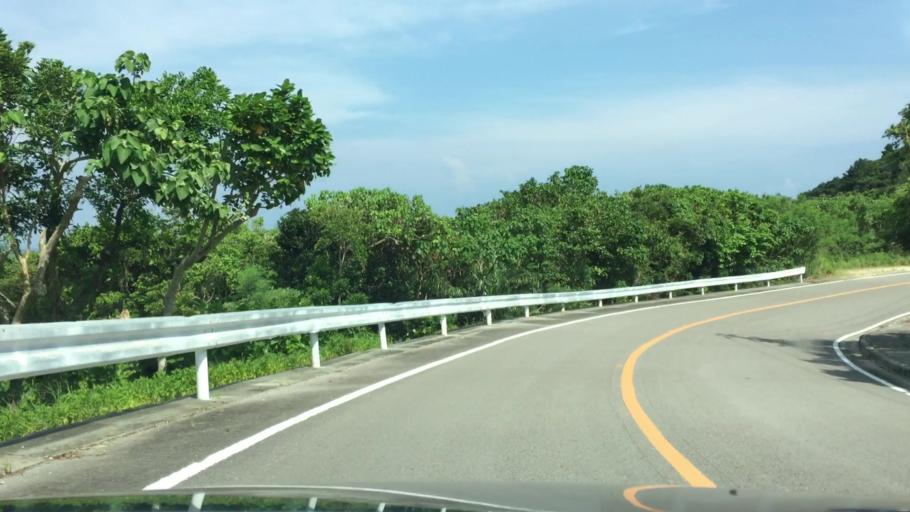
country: JP
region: Okinawa
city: Ishigaki
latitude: 24.5141
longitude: 124.2651
